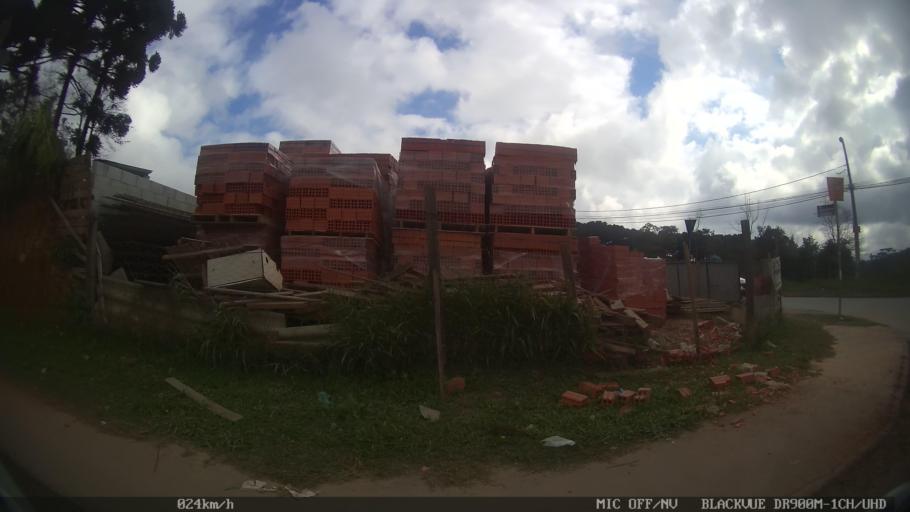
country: BR
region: Parana
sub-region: Colombo
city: Colombo
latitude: -25.3431
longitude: -49.2403
